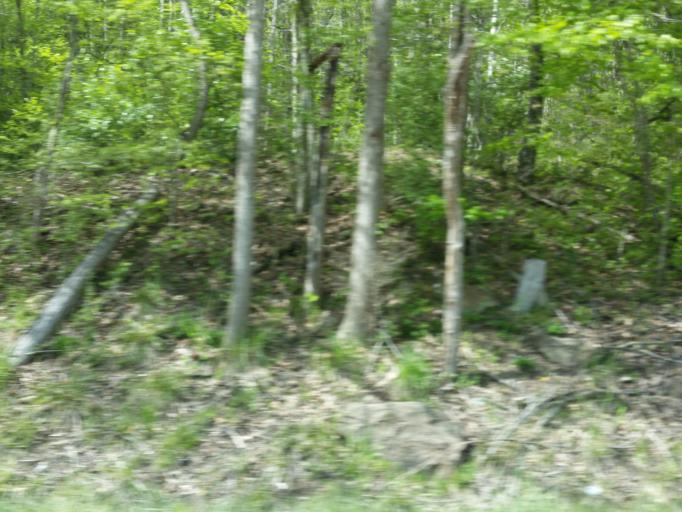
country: US
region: Kentucky
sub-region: Bell County
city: Middlesboro
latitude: 36.6145
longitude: -83.7696
